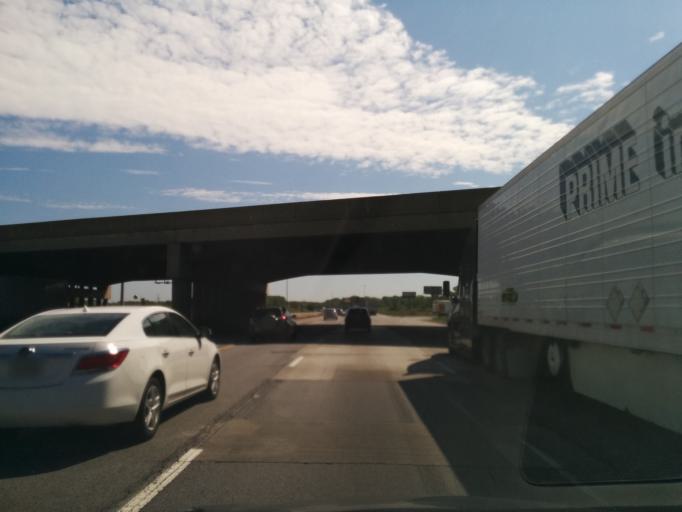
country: US
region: Indiana
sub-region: Lake County
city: Lake Station
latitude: 41.5828
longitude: -87.2408
